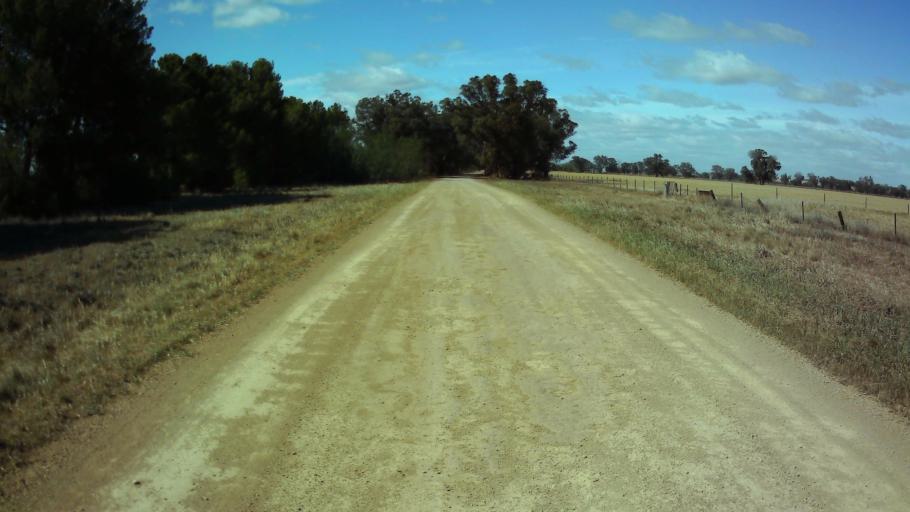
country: AU
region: New South Wales
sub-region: Weddin
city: Grenfell
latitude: -34.0351
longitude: 148.3167
